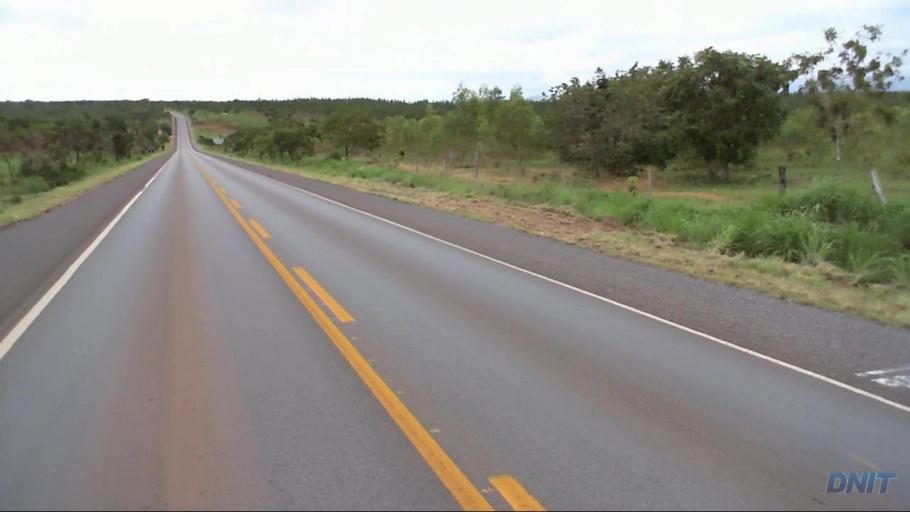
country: BR
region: Goias
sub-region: Barro Alto
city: Barro Alto
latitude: -15.2127
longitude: -48.6636
